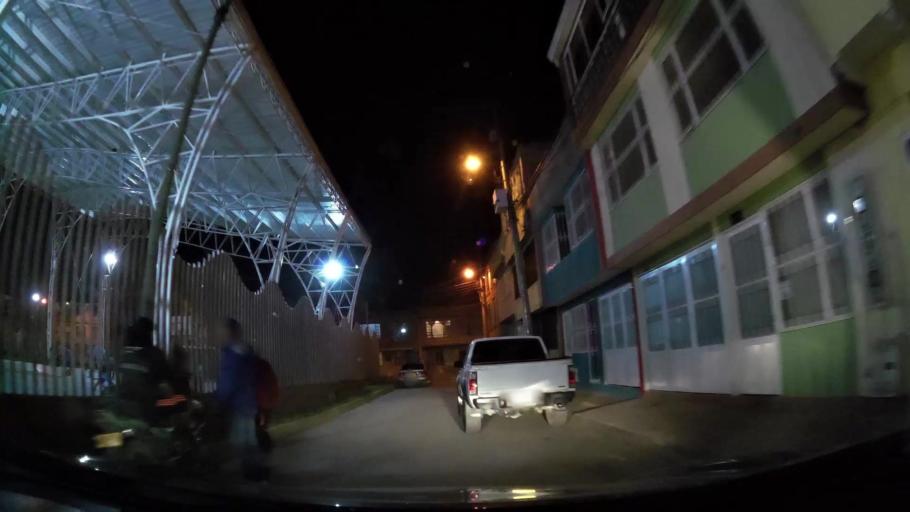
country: CO
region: Cundinamarca
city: Funza
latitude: 4.7185
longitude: -74.2156
